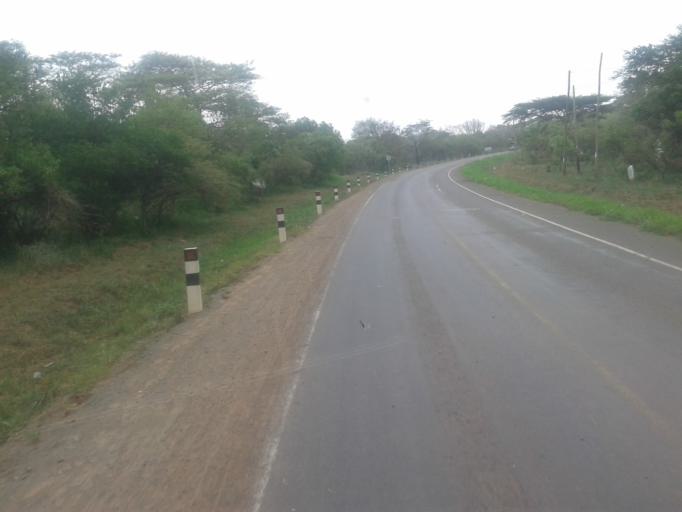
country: UG
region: Northern Region
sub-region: Oyam District
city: Oyam
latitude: 2.2485
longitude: 32.2357
